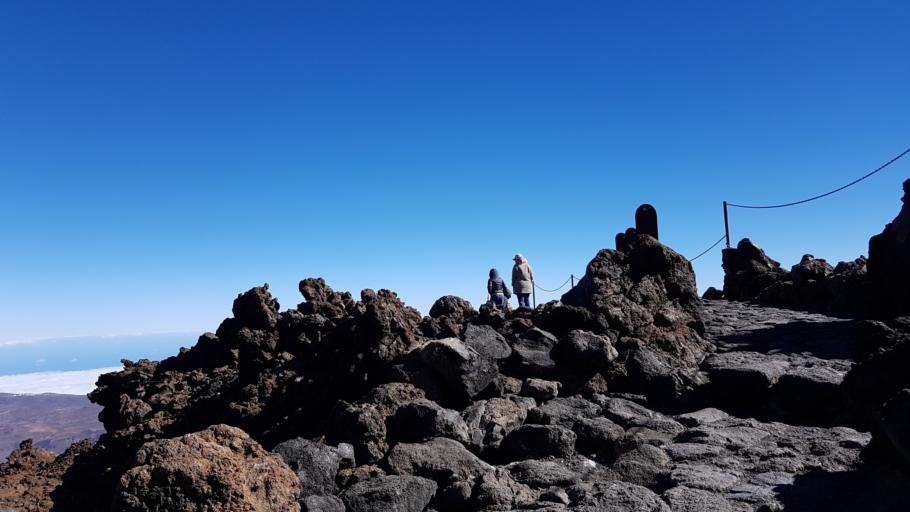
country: ES
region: Canary Islands
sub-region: Provincia de Santa Cruz de Tenerife
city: La Guancha
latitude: 28.2707
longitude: -16.6391
